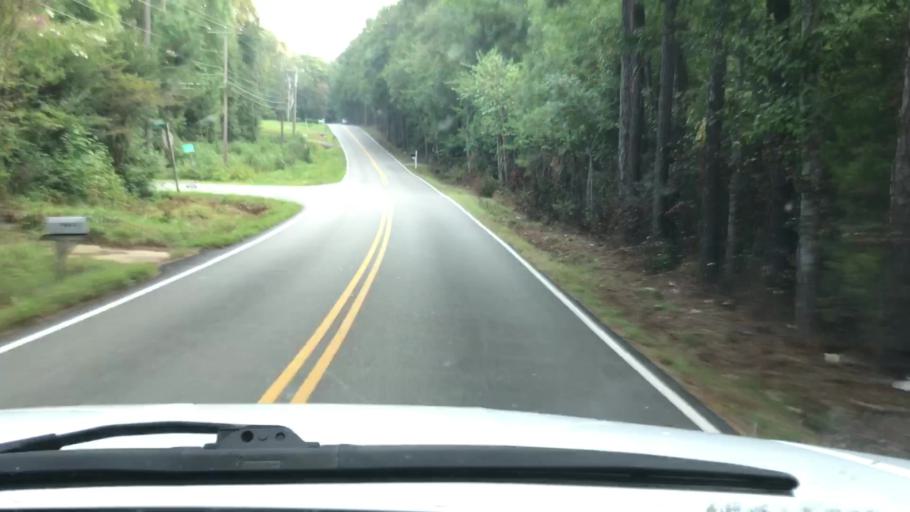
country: US
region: Virginia
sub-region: Chesterfield County
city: Chesterfield
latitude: 37.4339
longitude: -77.5281
